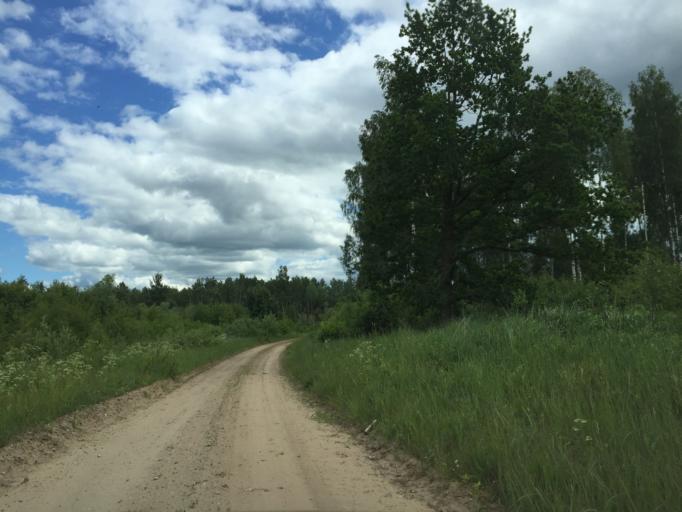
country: LV
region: Lecava
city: Iecava
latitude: 56.5663
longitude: 24.3052
